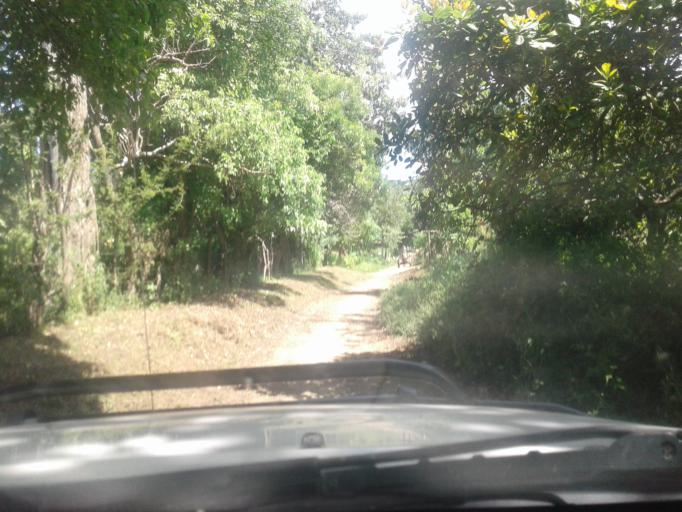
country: NI
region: Rivas
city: Tola
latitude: 11.4401
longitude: -85.9224
